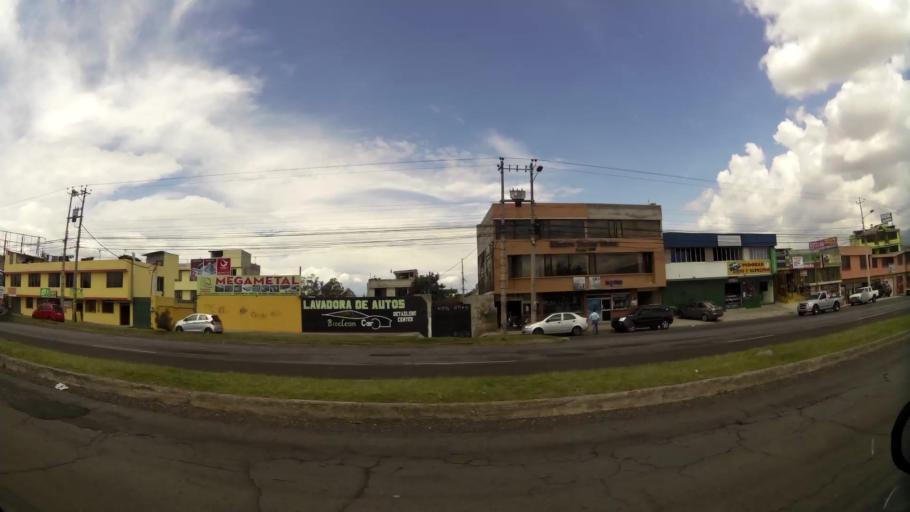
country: EC
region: Pichincha
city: Quito
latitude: -0.1047
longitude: -78.4291
